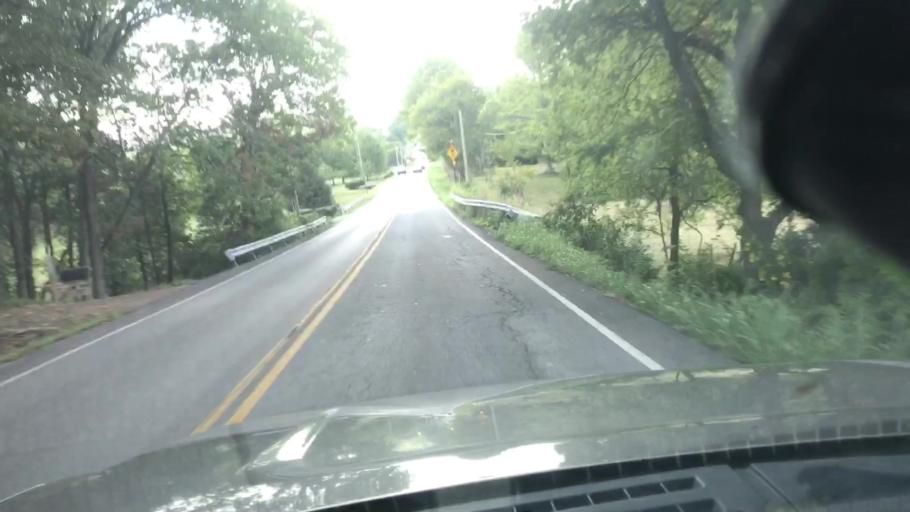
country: US
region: Tennessee
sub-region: Davidson County
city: Forest Hills
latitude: 36.0299
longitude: -86.9490
